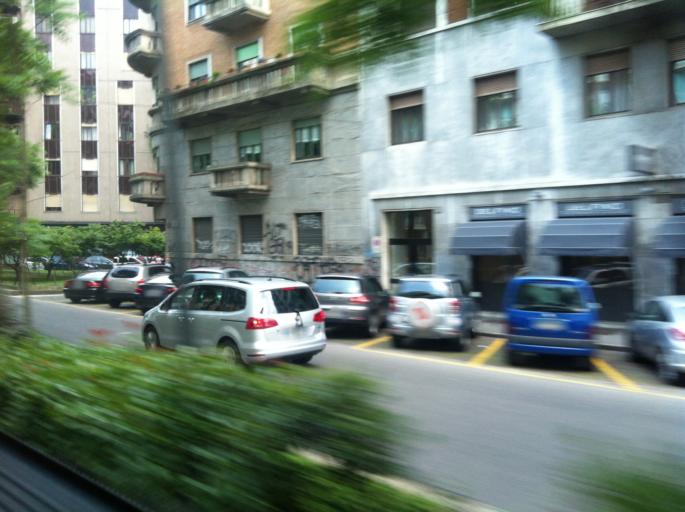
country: IT
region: Lombardy
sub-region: Citta metropolitana di Milano
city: Milano
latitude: 45.4823
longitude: 9.2197
